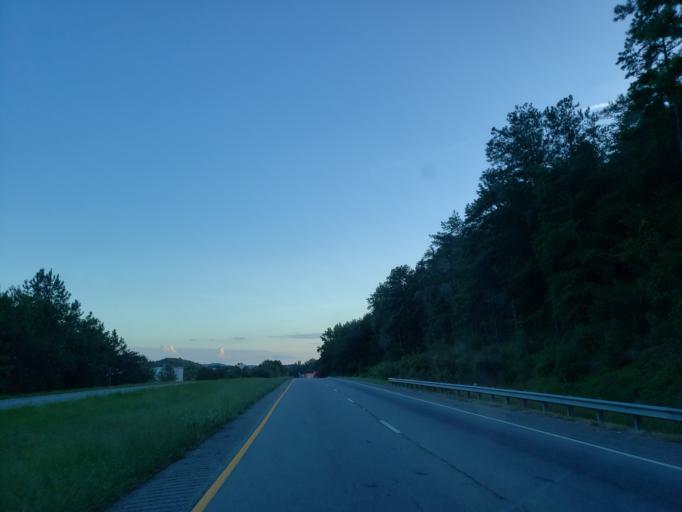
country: US
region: Georgia
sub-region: Floyd County
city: Lindale
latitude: 34.2052
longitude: -85.1929
